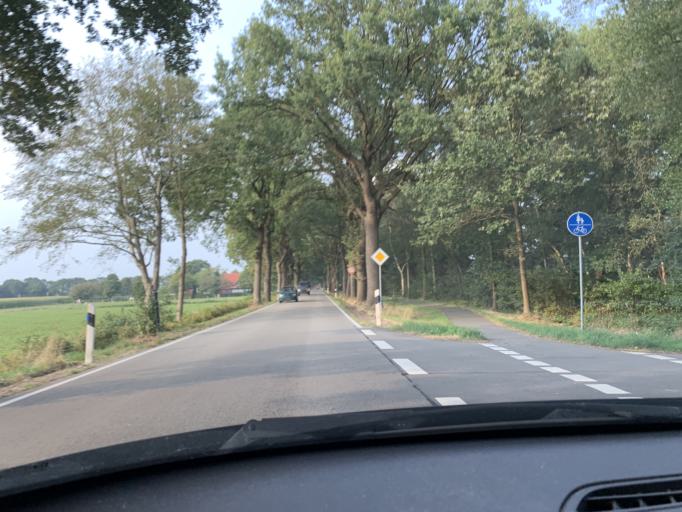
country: DE
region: Lower Saxony
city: Apen
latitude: 53.1841
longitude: 7.7818
